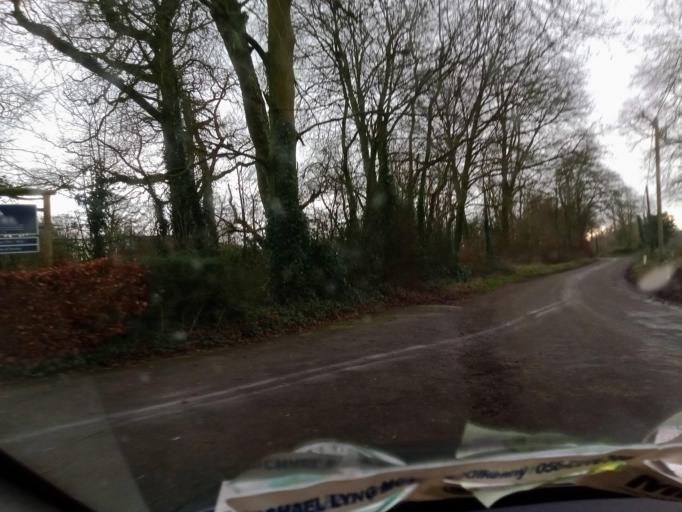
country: IE
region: Munster
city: Fethard
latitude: 52.5300
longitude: -7.7564
